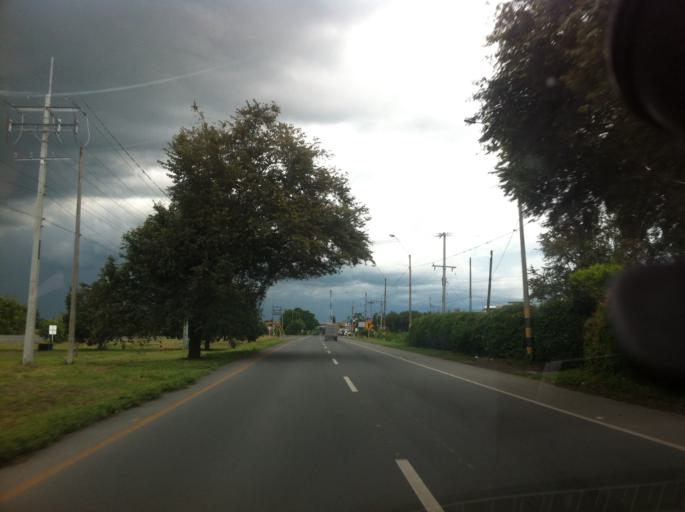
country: CO
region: Valle del Cauca
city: El Cerrito
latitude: 3.6979
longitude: -76.3168
